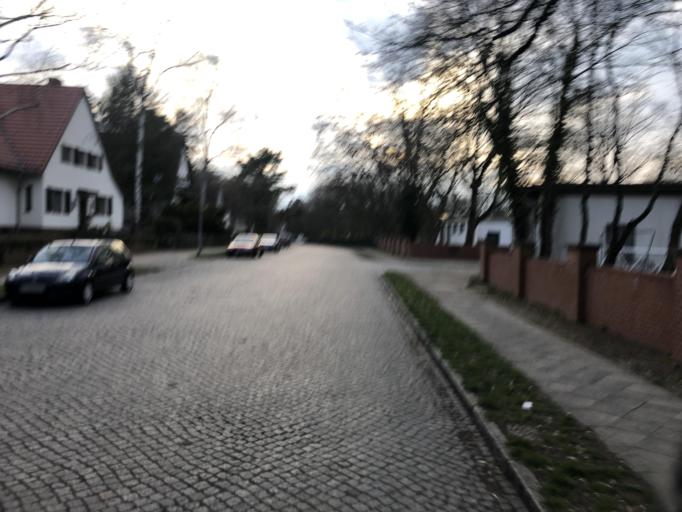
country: DE
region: Berlin
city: Frohnau
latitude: 52.6421
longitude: 13.2920
